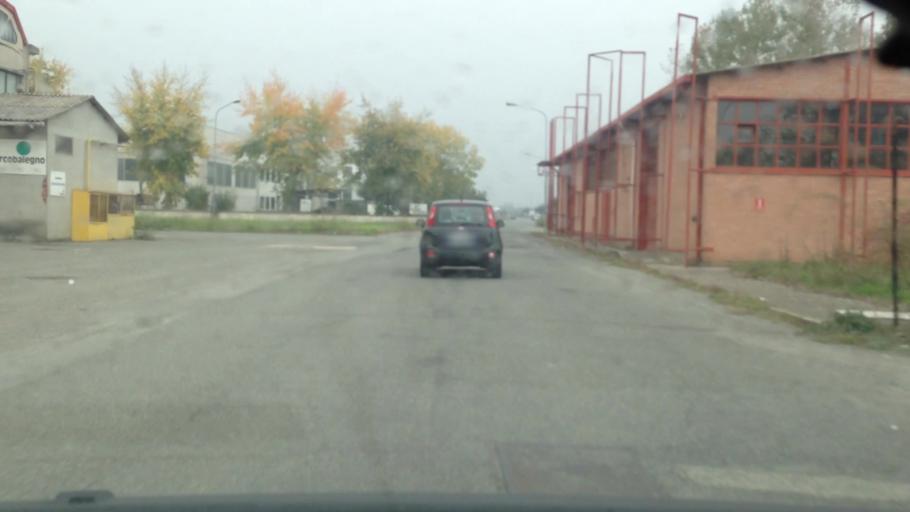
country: IT
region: Piedmont
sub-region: Provincia di Alessandria
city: Solero
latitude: 44.9144
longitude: 8.4826
